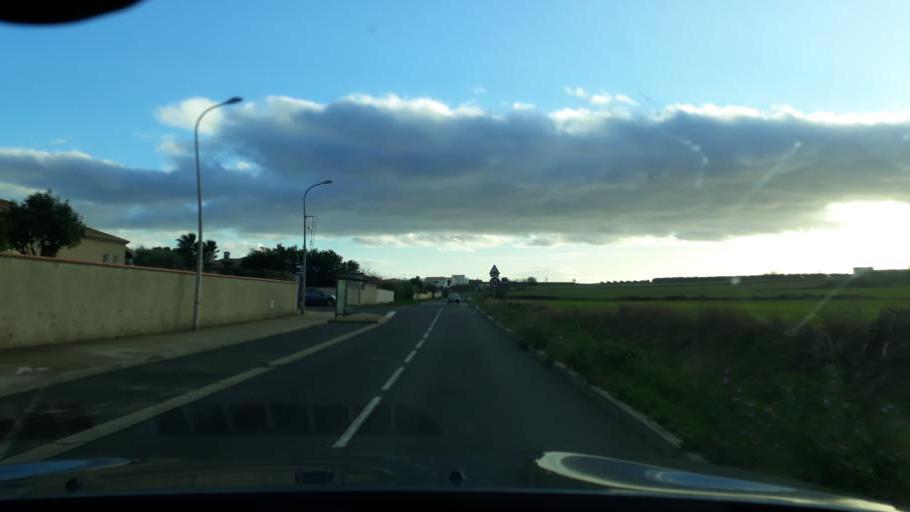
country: FR
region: Languedoc-Roussillon
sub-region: Departement de l'Herault
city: Colombiers
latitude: 43.3118
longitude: 3.1396
